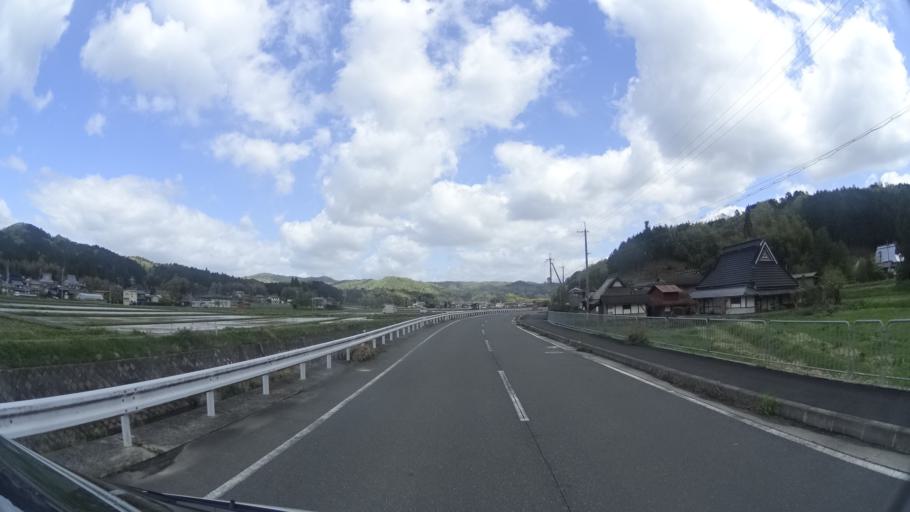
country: JP
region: Kyoto
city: Kameoka
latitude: 35.0963
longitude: 135.4583
